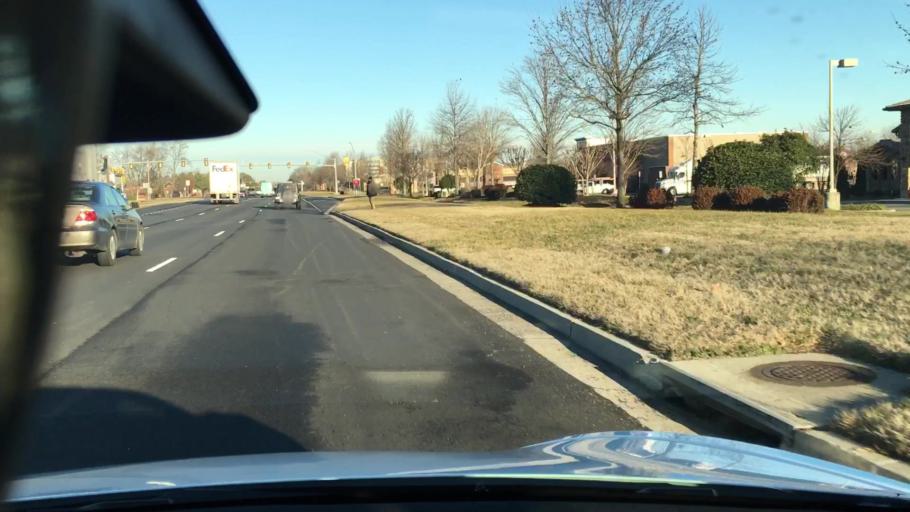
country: US
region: Virginia
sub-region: Henrico County
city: Montrose
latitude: 37.5257
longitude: -77.3544
